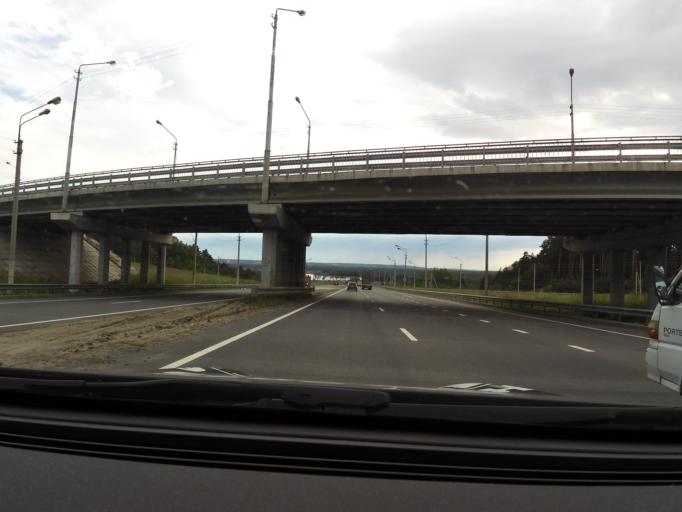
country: RU
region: Vladimir
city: Kommunar
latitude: 56.0567
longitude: 40.4404
